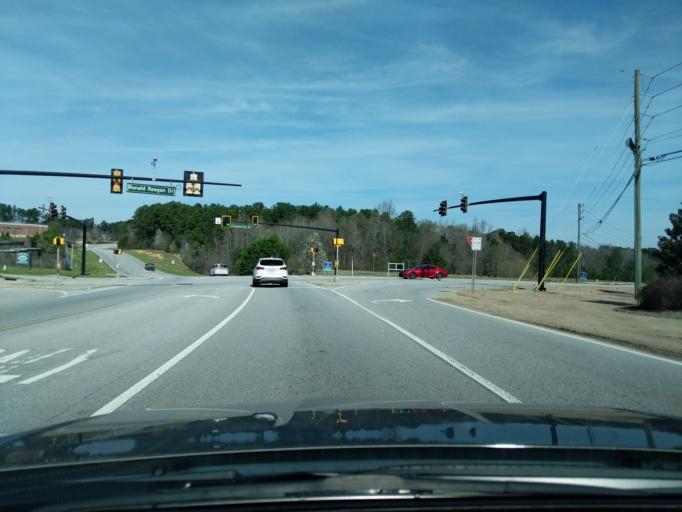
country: US
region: Georgia
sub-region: Columbia County
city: Evans
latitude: 33.5454
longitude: -82.1257
